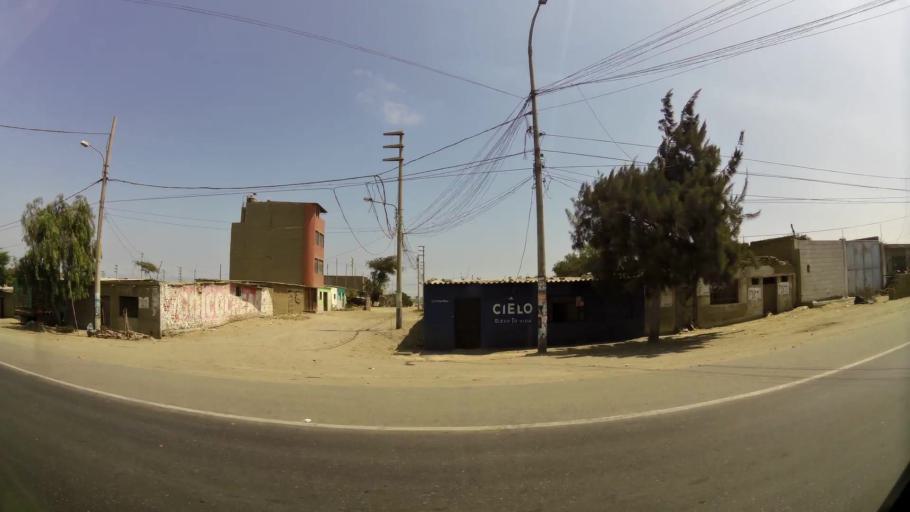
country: PE
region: La Libertad
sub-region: Provincia de Pacasmayo
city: Pacasmayo
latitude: -7.3993
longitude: -79.5584
